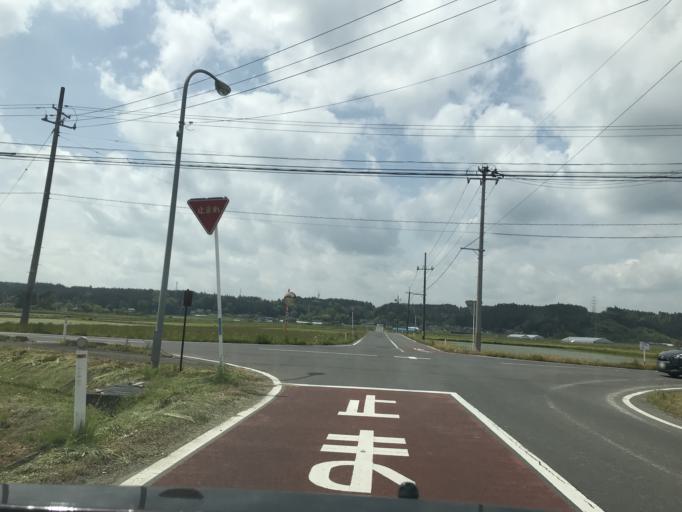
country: JP
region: Miyagi
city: Furukawa
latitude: 38.7480
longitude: 140.9343
